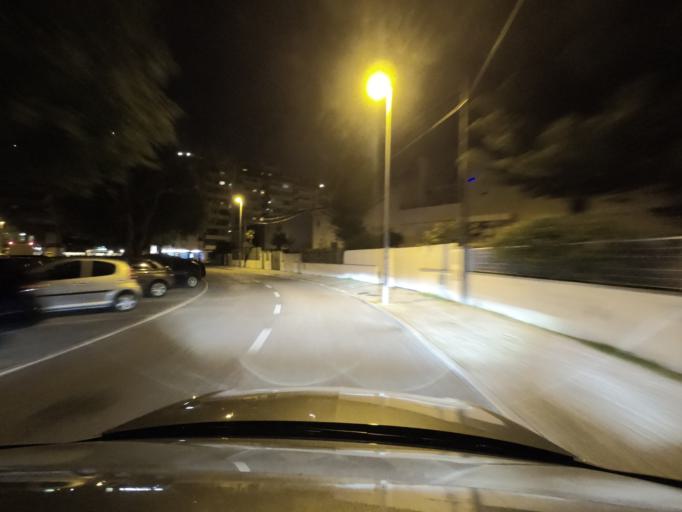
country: PT
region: Lisbon
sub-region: Oeiras
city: Carcavelos
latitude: 38.6923
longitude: -9.3255
